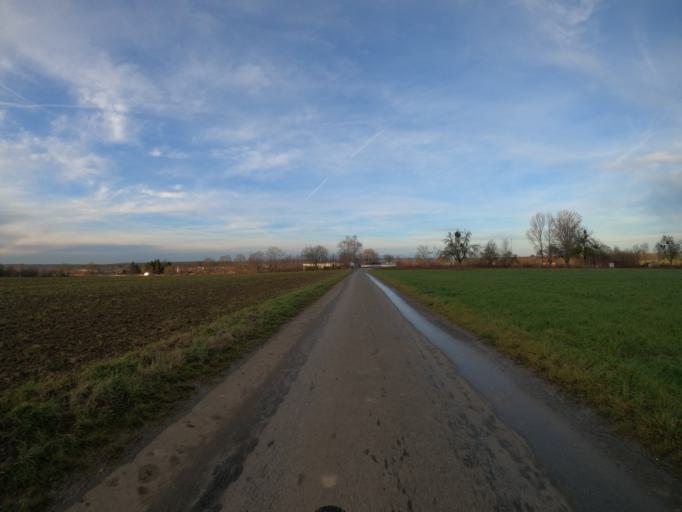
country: DE
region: Baden-Wuerttemberg
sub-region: Regierungsbezirk Stuttgart
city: Zell unter Aichelberg
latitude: 48.6420
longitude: 9.5821
